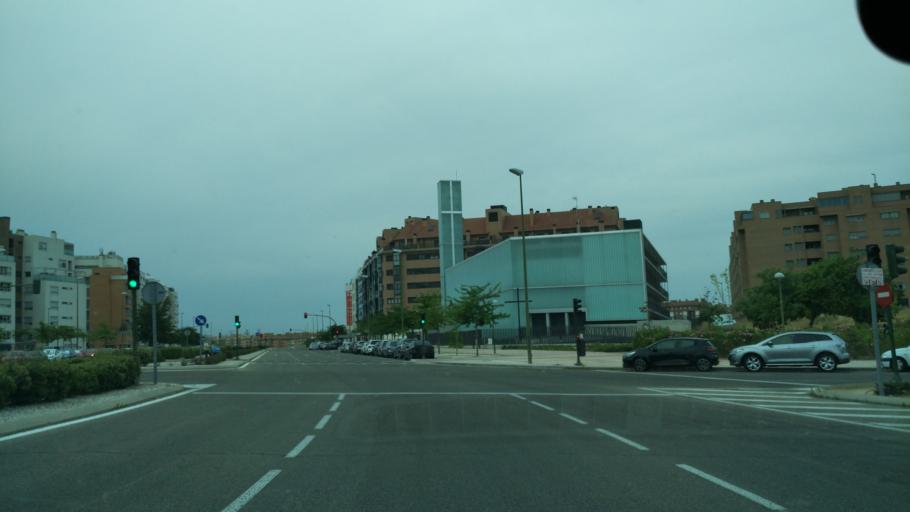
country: ES
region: Madrid
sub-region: Provincia de Madrid
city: Las Tablas
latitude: 40.5062
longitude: -3.6728
